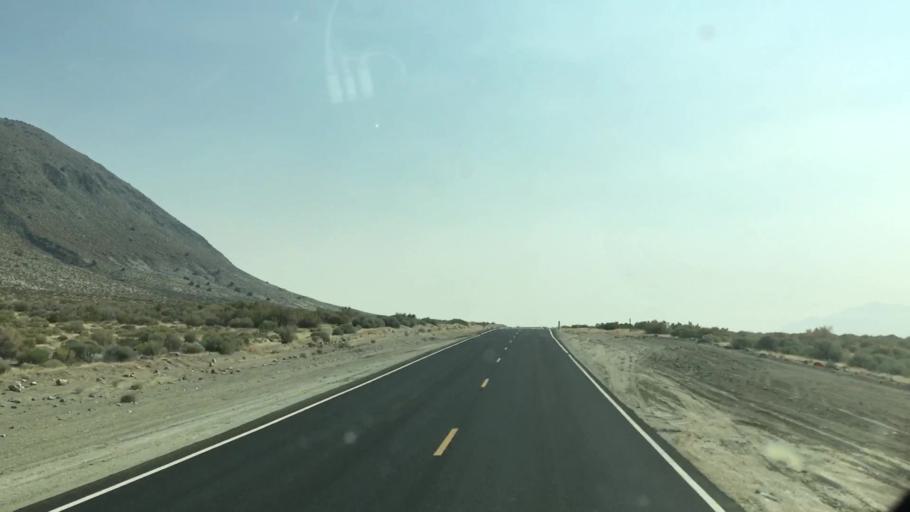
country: US
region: Nevada
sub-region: Pershing County
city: Lovelock
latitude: 40.7241
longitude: -119.3183
